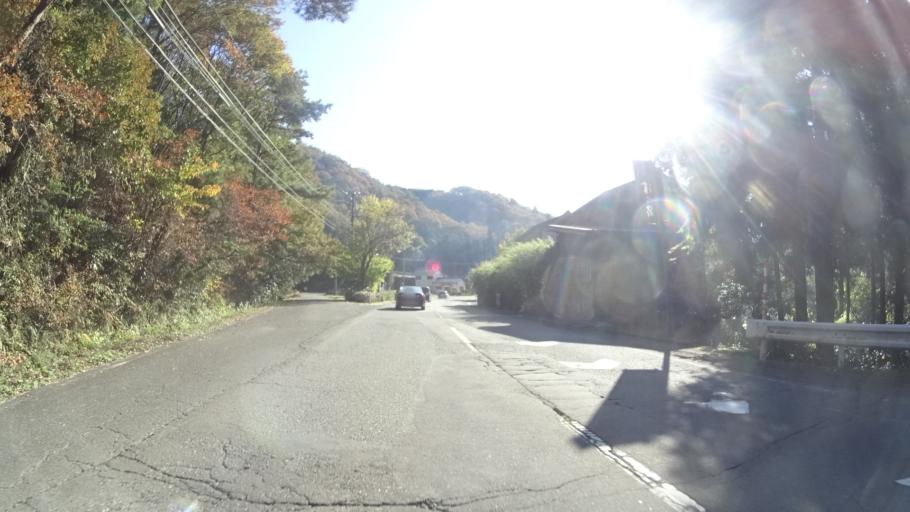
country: JP
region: Ishikawa
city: Komatsu
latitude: 36.3779
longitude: 136.5404
